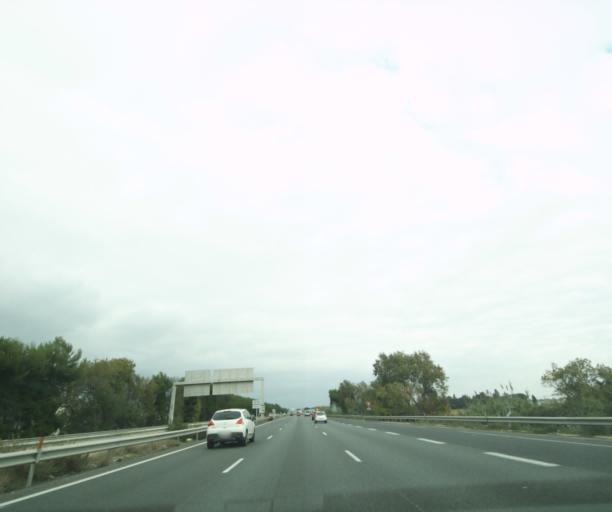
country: FR
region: Languedoc-Roussillon
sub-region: Departement de l'Herault
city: Lattes
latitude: 43.5762
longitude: 3.8791
